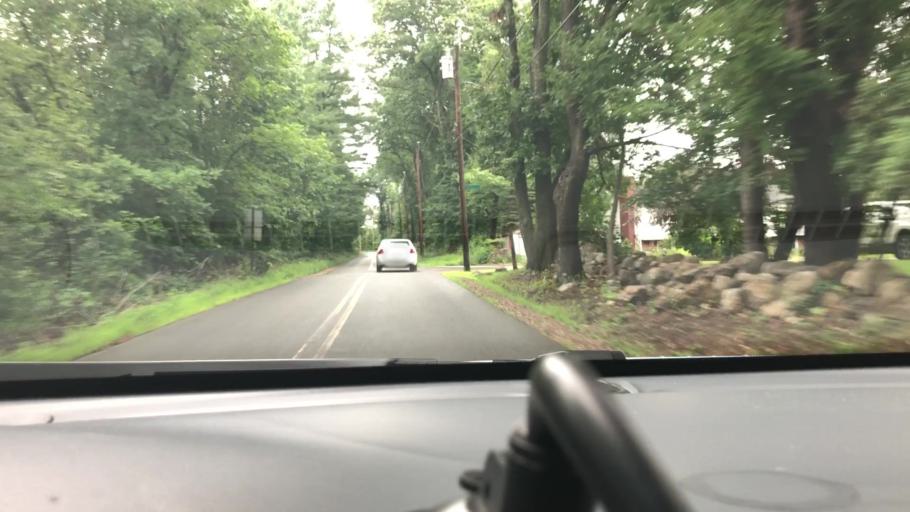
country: US
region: New Hampshire
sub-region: Hillsborough County
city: Pinardville
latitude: 42.9865
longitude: -71.5197
